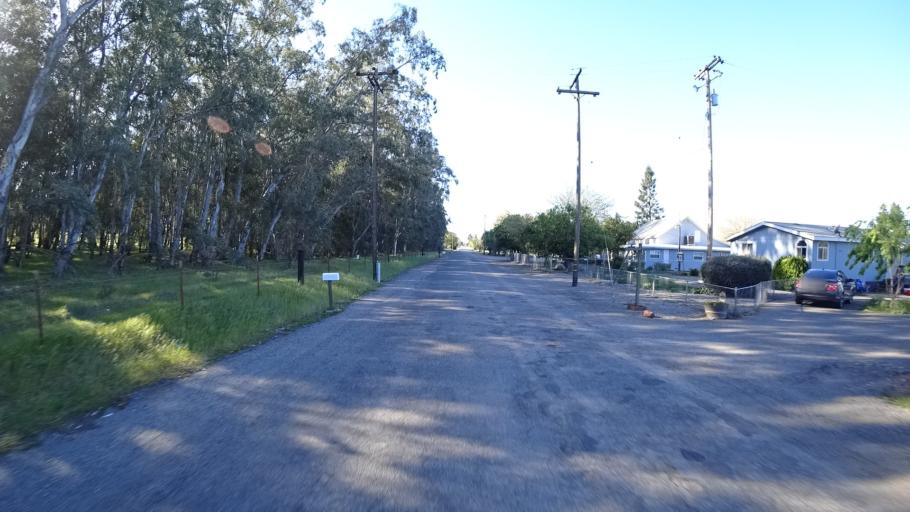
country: US
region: California
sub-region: Glenn County
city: Orland
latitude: 39.7637
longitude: -122.2155
